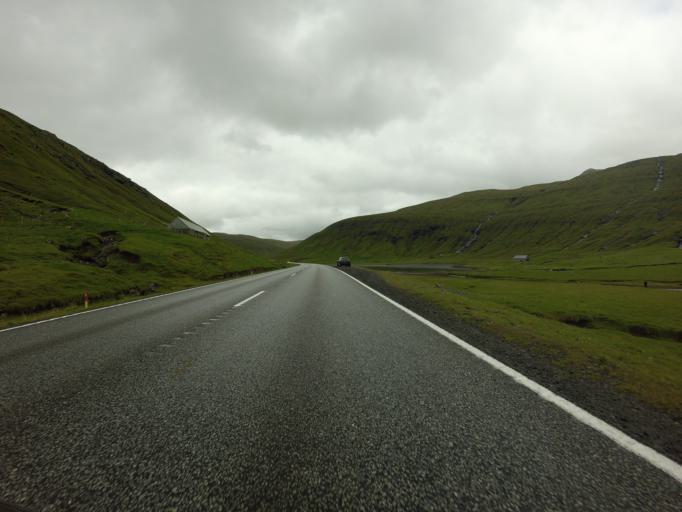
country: FO
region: Streymoy
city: Kollafjordhur
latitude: 62.1252
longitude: -6.9977
